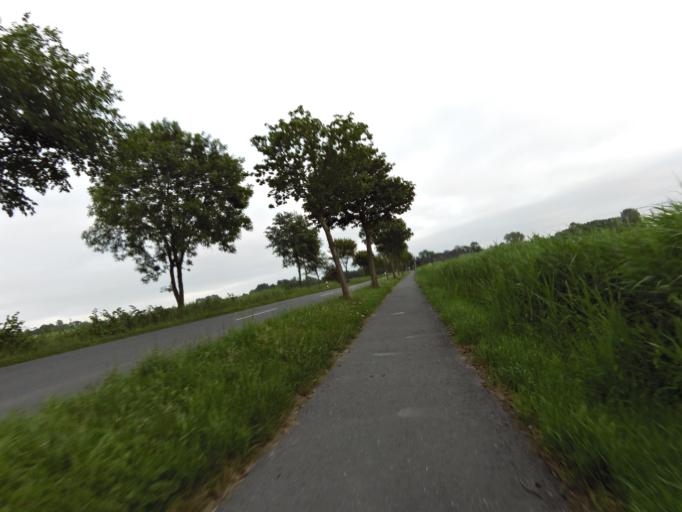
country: DE
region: Lower Saxony
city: Padingbuttel
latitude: 53.7131
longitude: 8.5500
